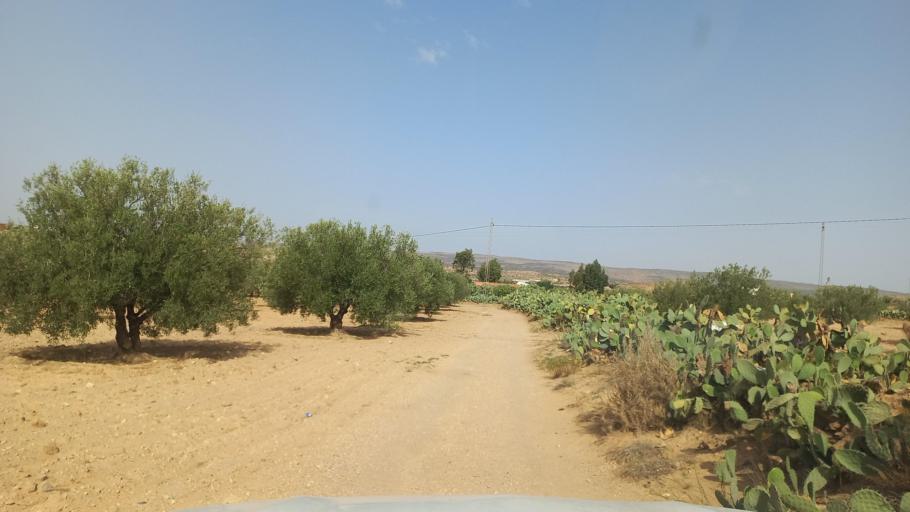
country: TN
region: Al Qasrayn
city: Kasserine
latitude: 35.2984
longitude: 8.9590
